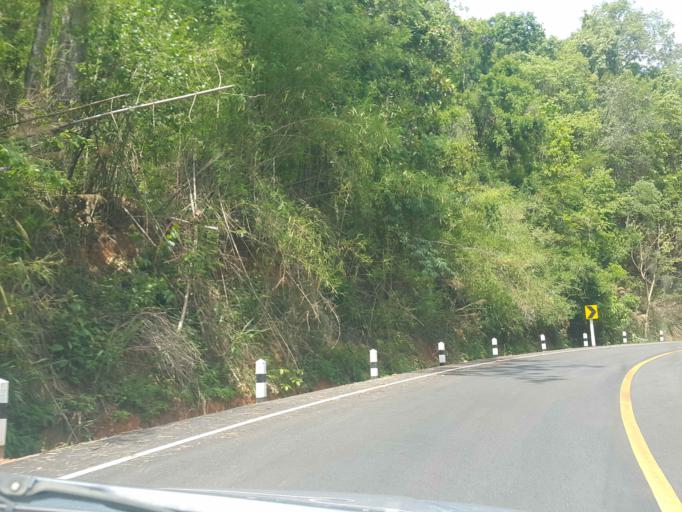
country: TH
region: Nan
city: Ban Luang
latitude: 18.8739
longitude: 100.5067
